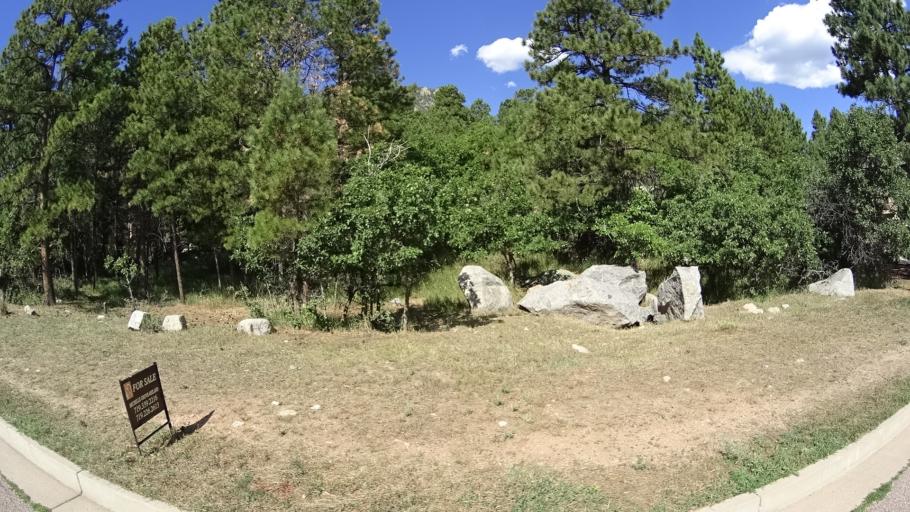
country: US
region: Colorado
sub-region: El Paso County
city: Fort Carson
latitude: 38.7478
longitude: -104.8372
